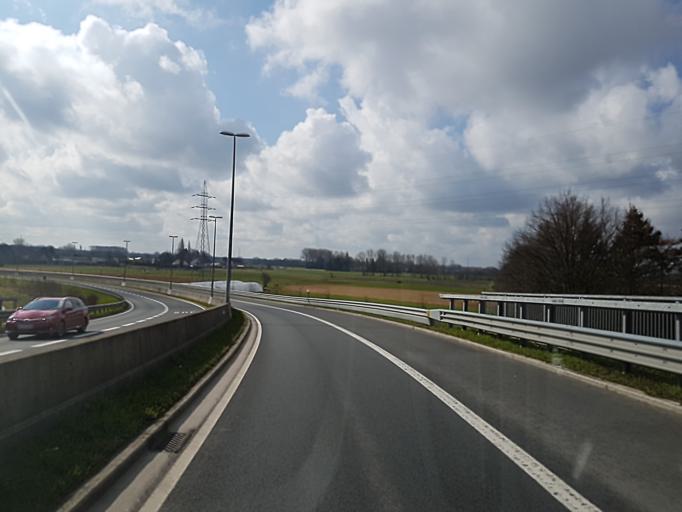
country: BE
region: Flanders
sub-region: Provincie Oost-Vlaanderen
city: Sint-Niklaas
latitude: 51.1579
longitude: 4.1080
